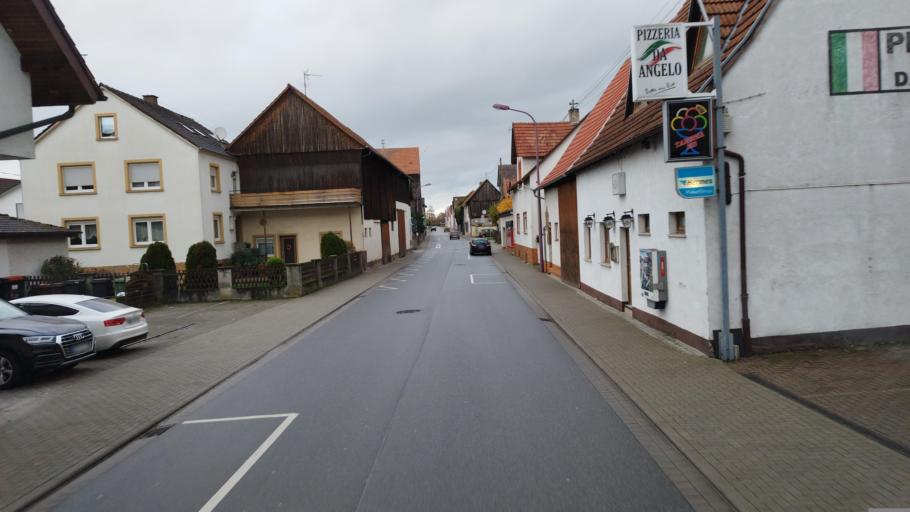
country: DE
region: Rheinland-Pfalz
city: Hatzenbuhl
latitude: 49.1111
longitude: 8.2435
